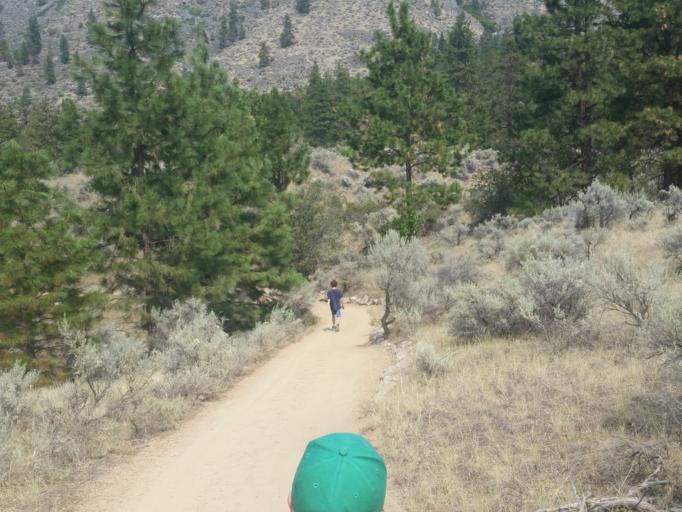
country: CA
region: British Columbia
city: Osoyoos
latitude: 49.0439
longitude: -119.4348
